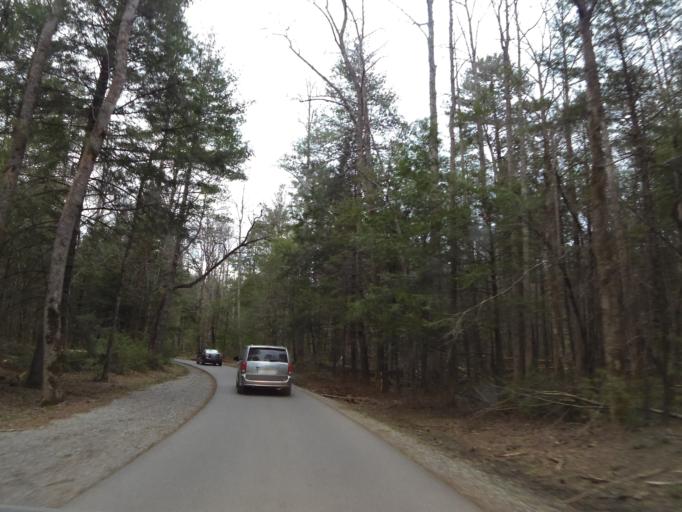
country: US
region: Tennessee
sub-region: Blount County
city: Wildwood
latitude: 35.5902
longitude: -83.7982
